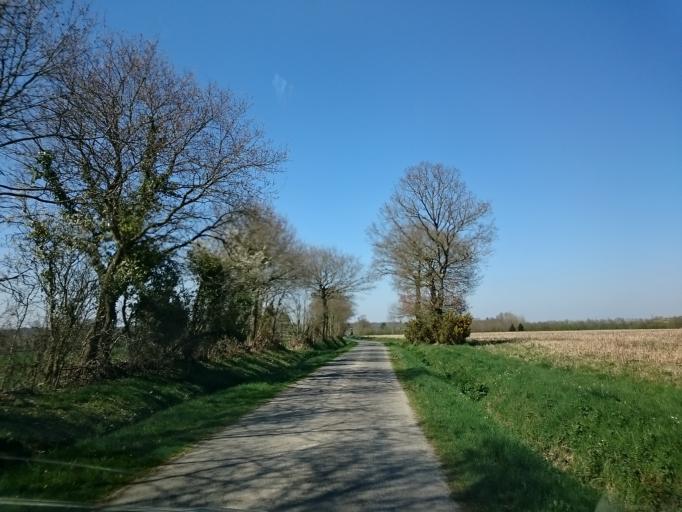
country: FR
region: Brittany
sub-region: Departement d'Ille-et-Vilaine
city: Chanteloup
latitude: 47.9539
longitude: -1.6429
